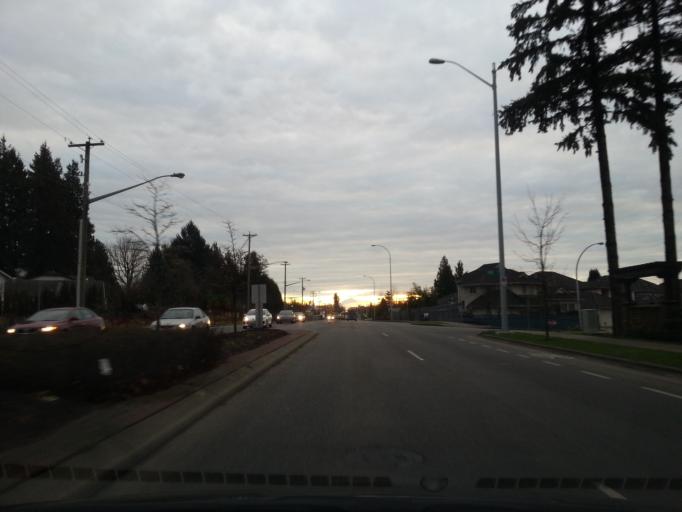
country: CA
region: British Columbia
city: Surrey
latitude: 49.1683
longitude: -122.8072
